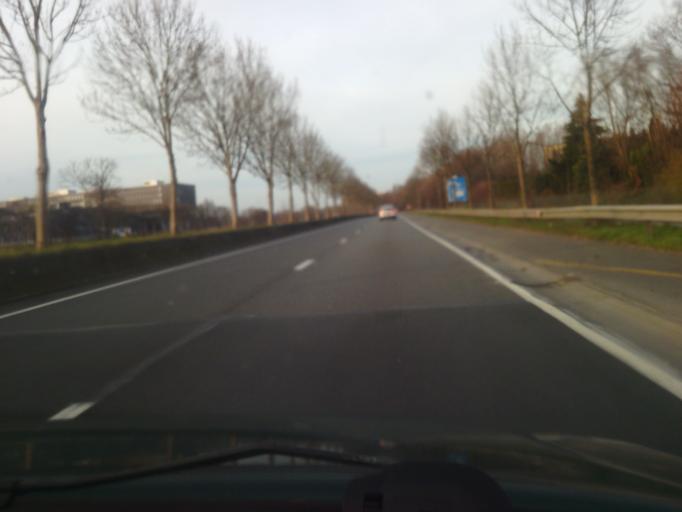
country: BE
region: Flanders
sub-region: Provincie Oost-Vlaanderen
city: Gent
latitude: 51.0244
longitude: 3.7042
